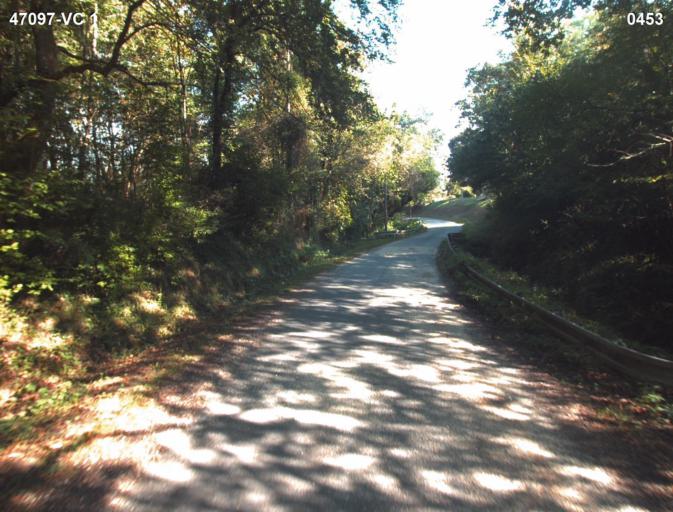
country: FR
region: Aquitaine
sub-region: Departement du Lot-et-Garonne
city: Vianne
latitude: 44.2178
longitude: 0.3485
